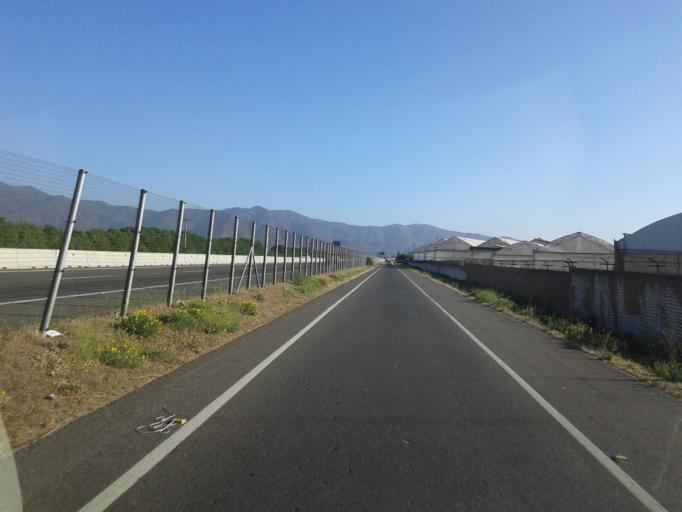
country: CL
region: Valparaiso
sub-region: Provincia de Quillota
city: Quillota
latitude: -32.8501
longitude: -71.2245
